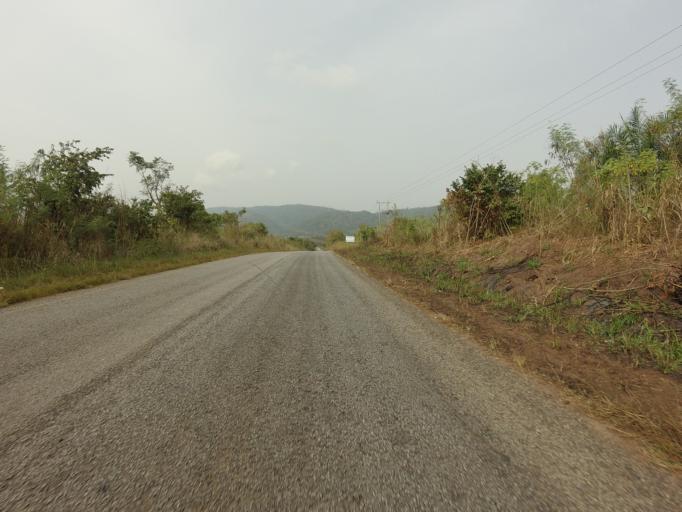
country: GH
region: Volta
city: Ho
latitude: 6.5751
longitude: 0.3233
